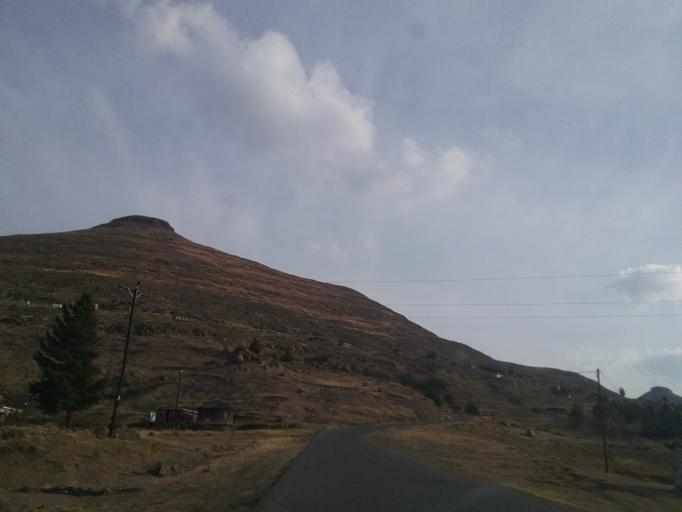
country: LS
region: Quthing
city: Quthing
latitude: -30.1938
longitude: 28.1184
